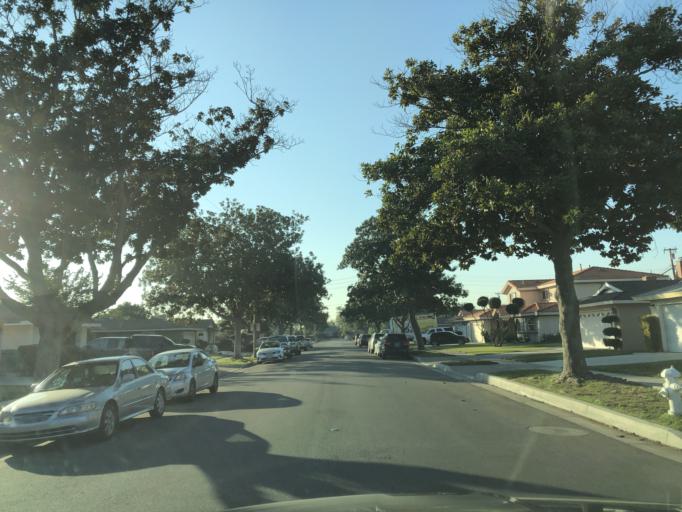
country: US
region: California
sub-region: Orange County
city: Orange
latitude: 33.7646
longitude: -117.8450
